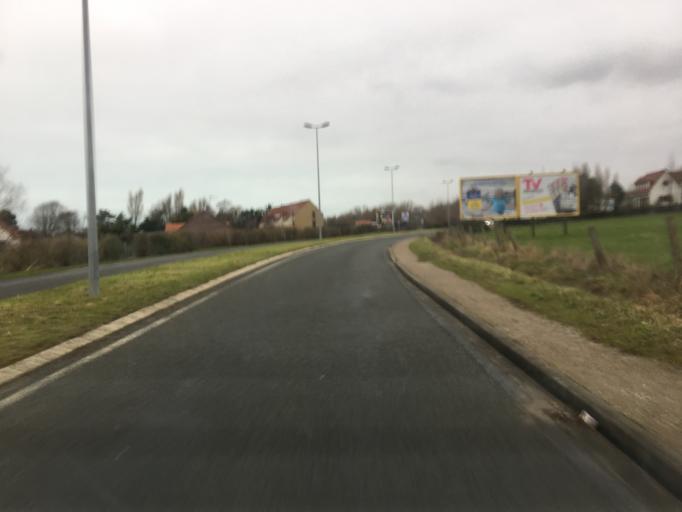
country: FR
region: Nord-Pas-de-Calais
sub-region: Departement du Pas-de-Calais
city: Le Portel
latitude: 50.6960
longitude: 1.5792
